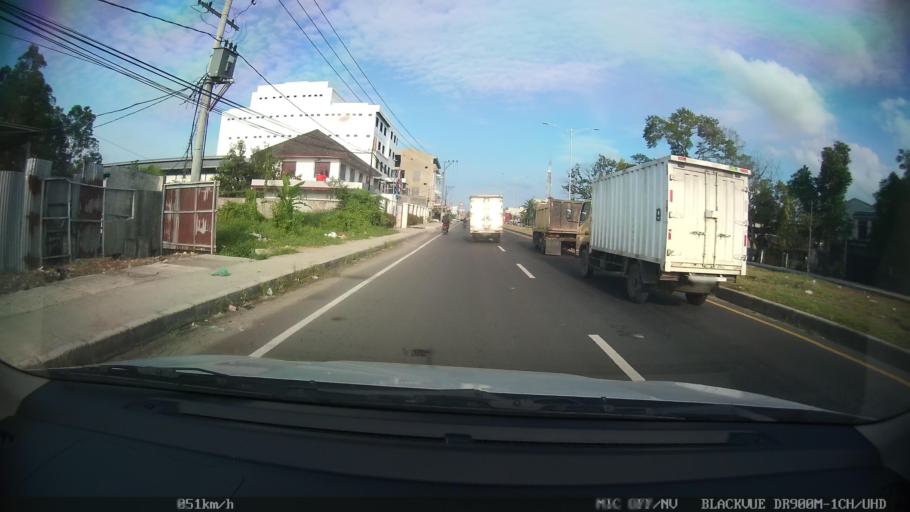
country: ID
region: North Sumatra
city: Medan
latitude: 3.6157
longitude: 98.6406
